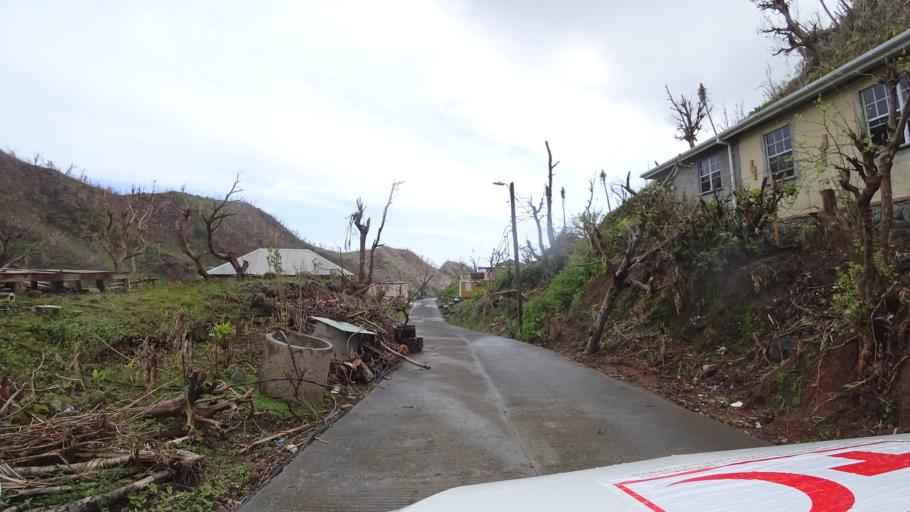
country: DM
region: Saint David
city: Castle Bruce
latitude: 15.4134
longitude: -61.2562
